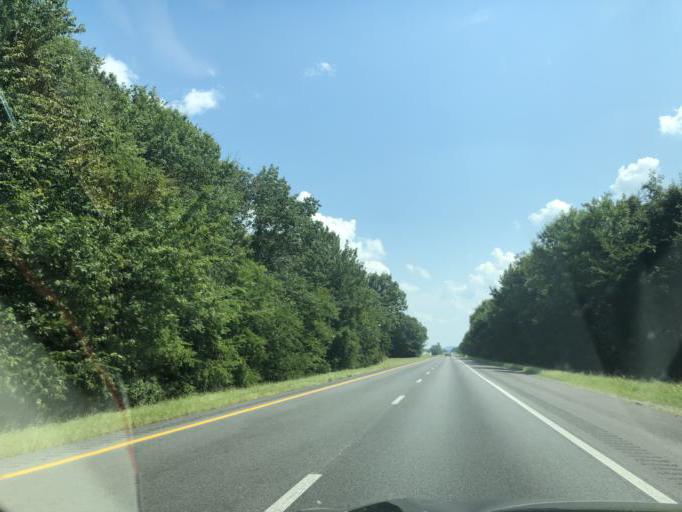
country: US
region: Tennessee
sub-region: Rutherford County
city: Plainview
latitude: 35.7363
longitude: -86.3320
